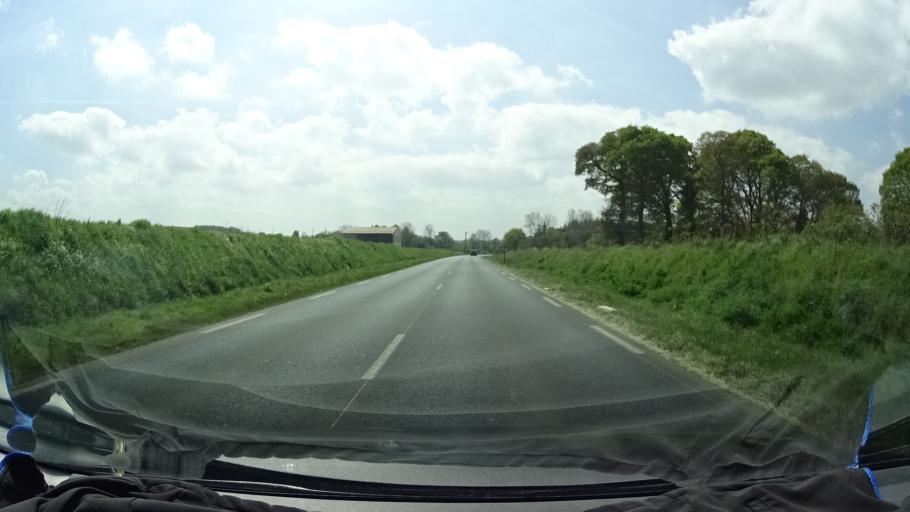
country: FR
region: Brittany
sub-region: Departement des Cotes-d'Armor
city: Goudelin
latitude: 48.5889
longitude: -3.0486
